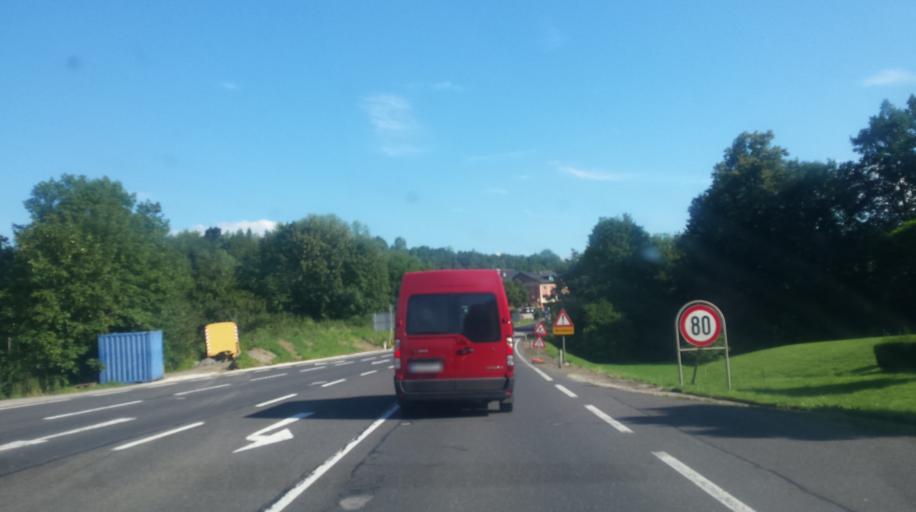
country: AT
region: Upper Austria
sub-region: Politischer Bezirk Vocklabruck
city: Attnang-Puchheim
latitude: 47.9822
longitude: 13.6994
